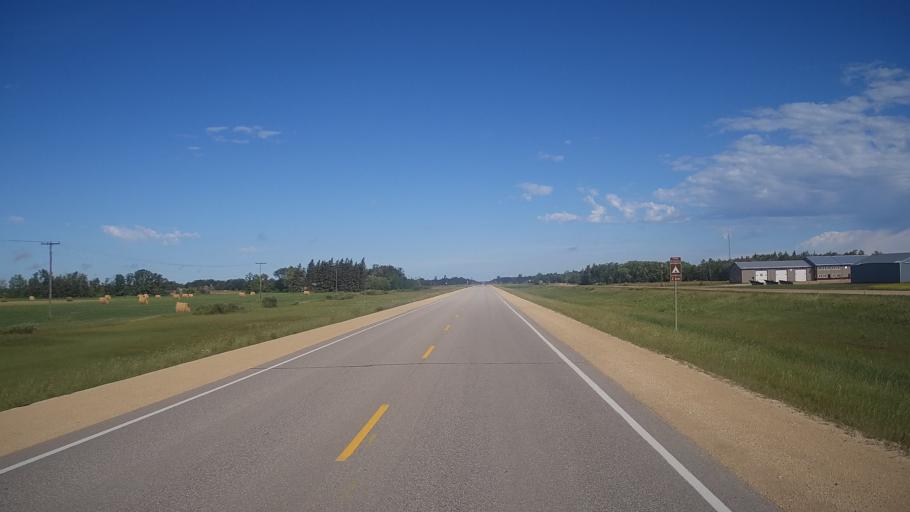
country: CA
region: Manitoba
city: Stonewall
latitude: 50.1992
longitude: -97.6500
